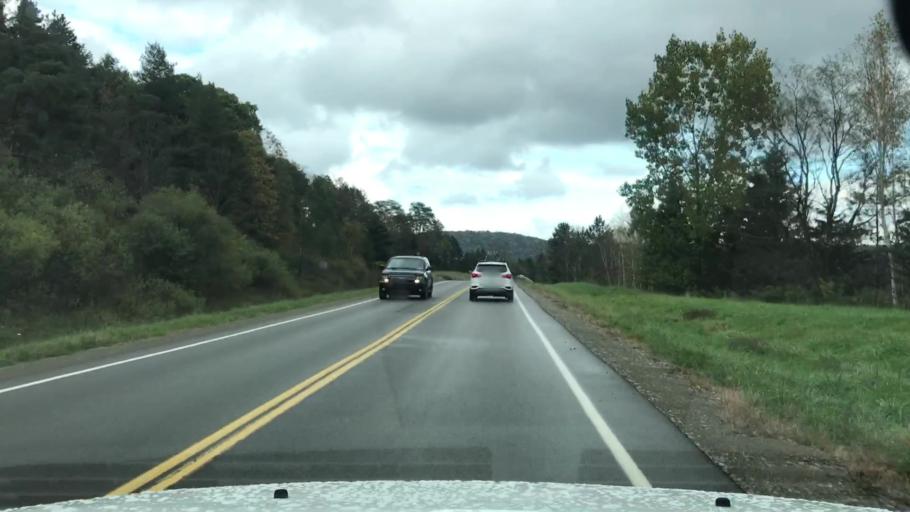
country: US
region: New York
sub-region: Cattaraugus County
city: Salamanca
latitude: 42.2637
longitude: -78.6729
